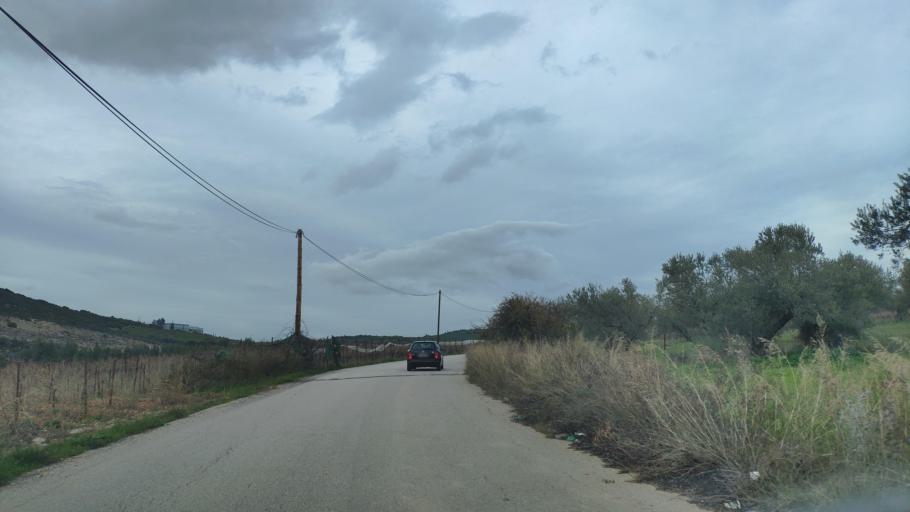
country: GR
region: Peloponnese
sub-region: Nomos Korinthias
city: Nemea
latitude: 37.7978
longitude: 22.7263
